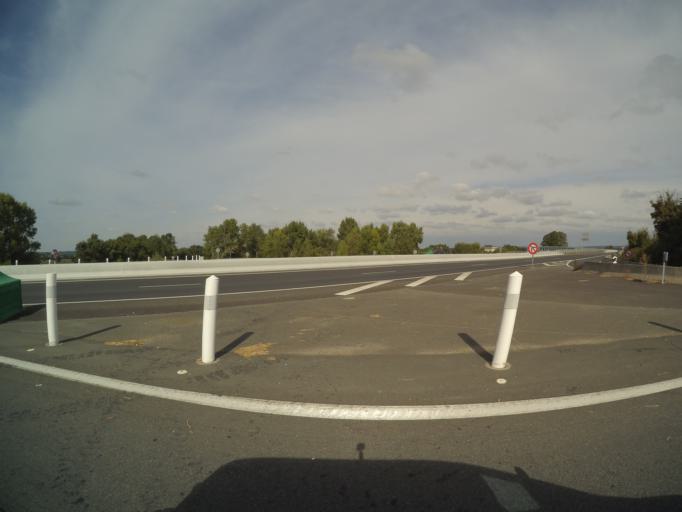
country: FR
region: Pays de la Loire
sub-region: Departement de Maine-et-Loire
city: Saumur
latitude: 47.2731
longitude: -0.0808
